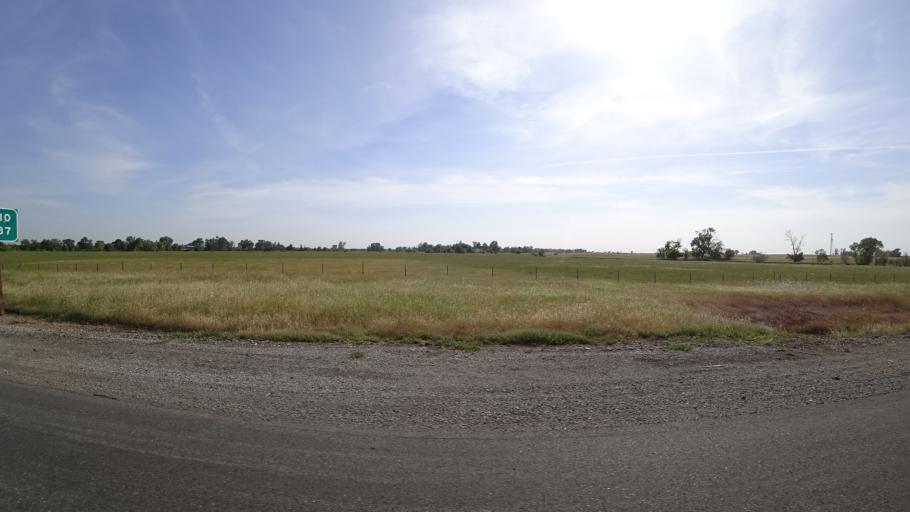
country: US
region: California
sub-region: Butte County
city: Durham
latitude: 39.6112
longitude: -121.6766
